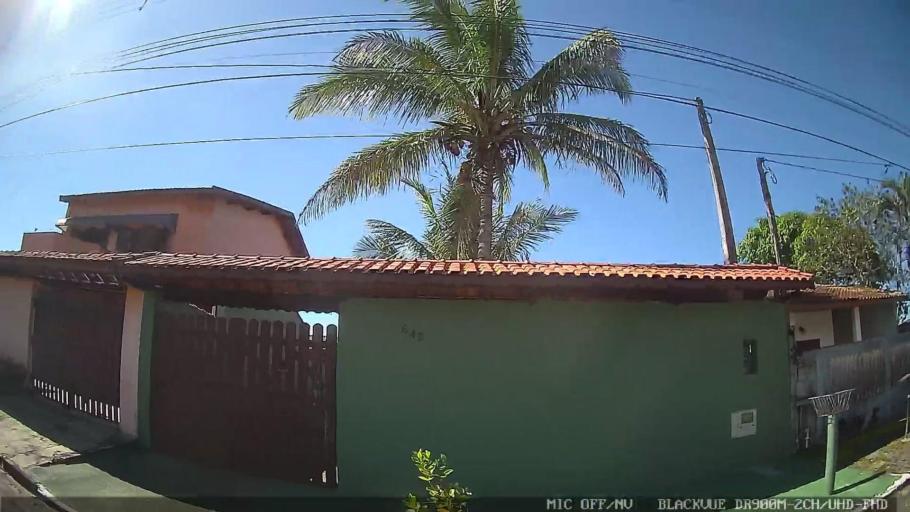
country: BR
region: Sao Paulo
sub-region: Itanhaem
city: Itanhaem
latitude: -24.2235
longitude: -46.8668
